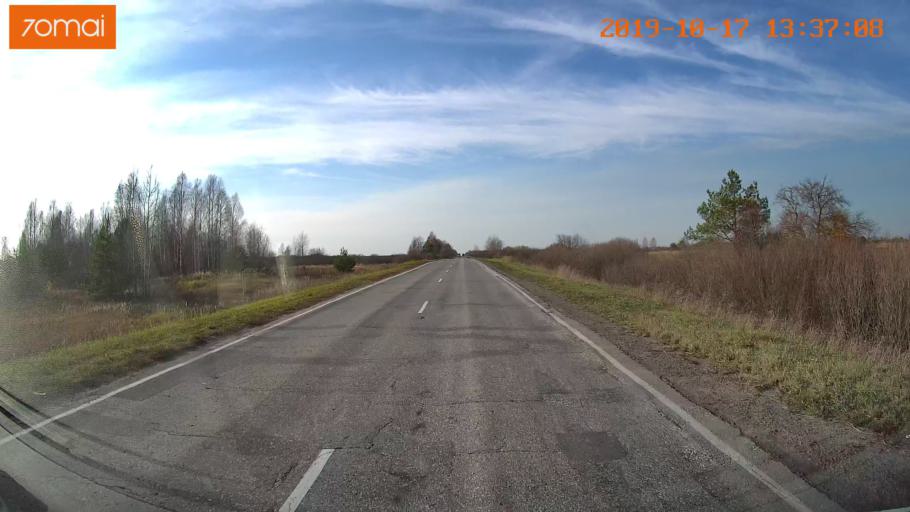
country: RU
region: Rjazan
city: Tuma
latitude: 55.1409
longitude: 40.6467
